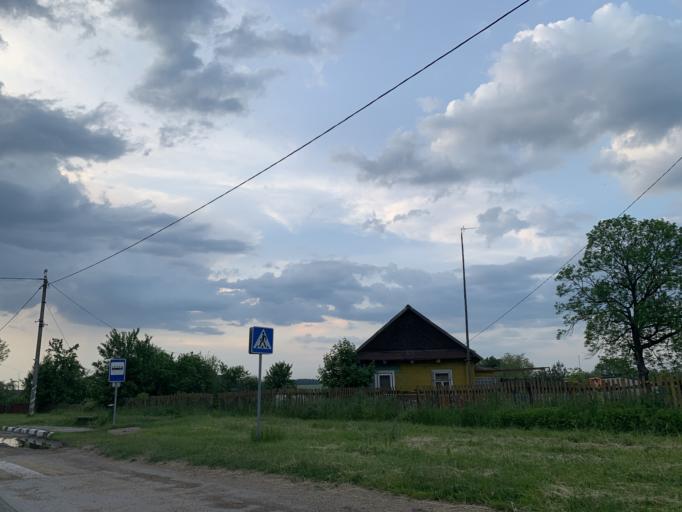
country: BY
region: Minsk
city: Tsimkavichy
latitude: 53.1258
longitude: 26.8822
